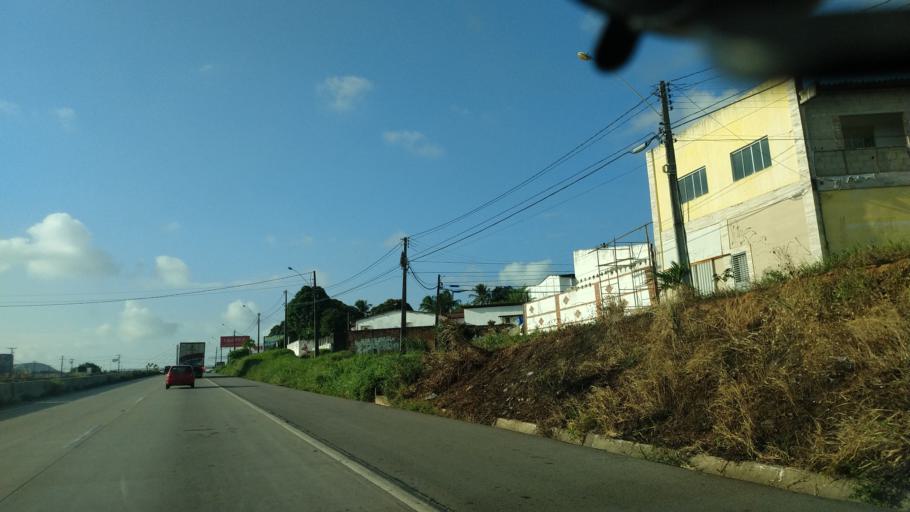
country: BR
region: Rio Grande do Norte
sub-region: Parnamirim
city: Parnamirim
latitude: -5.9313
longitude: -35.2647
